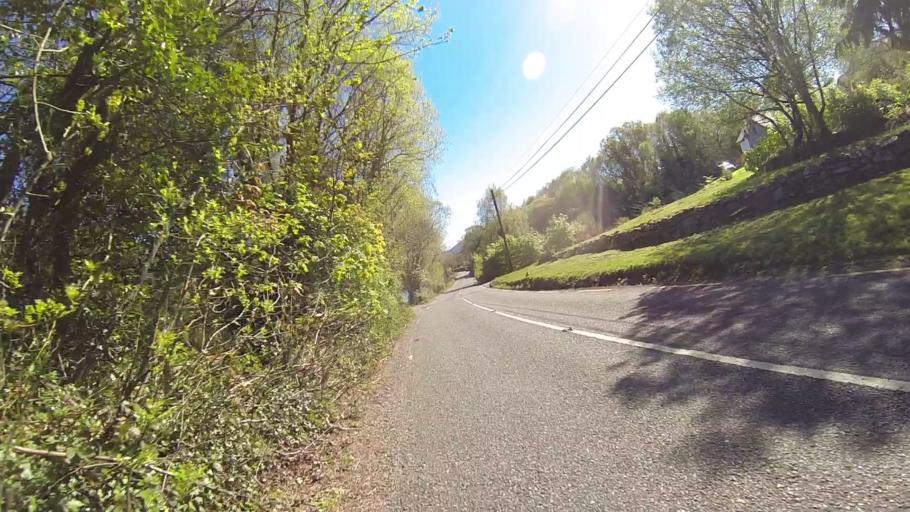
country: IE
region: Munster
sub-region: Ciarrai
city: Kenmare
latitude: 51.8427
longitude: -9.6633
